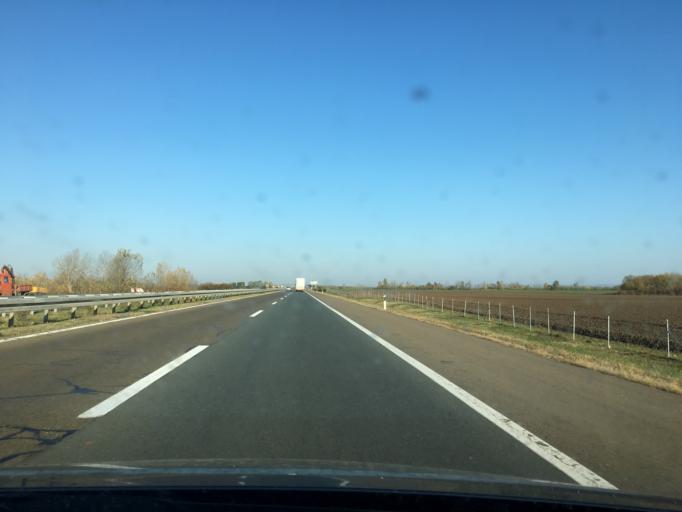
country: RS
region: Autonomna Pokrajina Vojvodina
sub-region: Sremski Okrug
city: Stara Pazova
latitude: 45.0188
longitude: 20.1945
